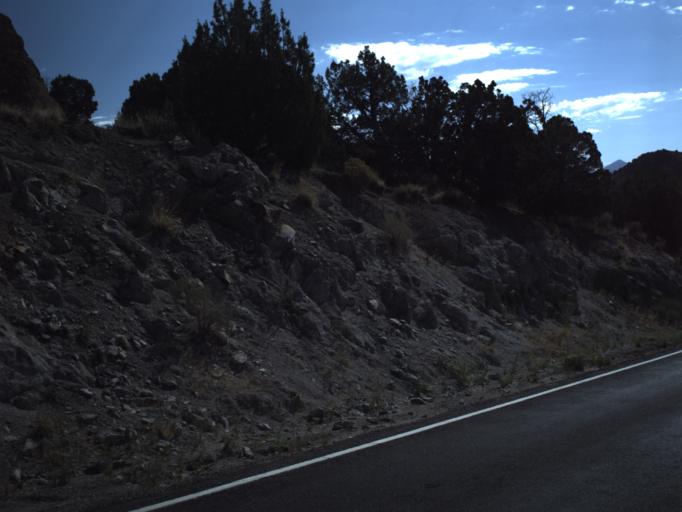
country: US
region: Utah
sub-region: Utah County
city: Genola
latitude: 39.9679
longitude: -112.0535
